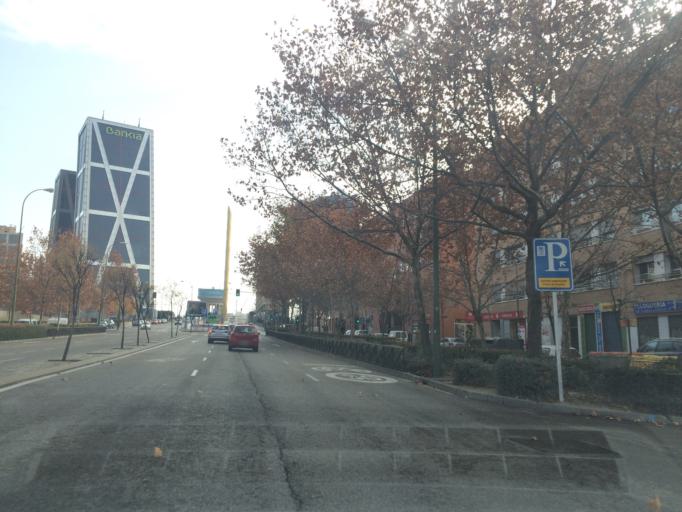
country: ES
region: Madrid
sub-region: Provincia de Madrid
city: Chamartin
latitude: 40.4683
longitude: -3.6940
